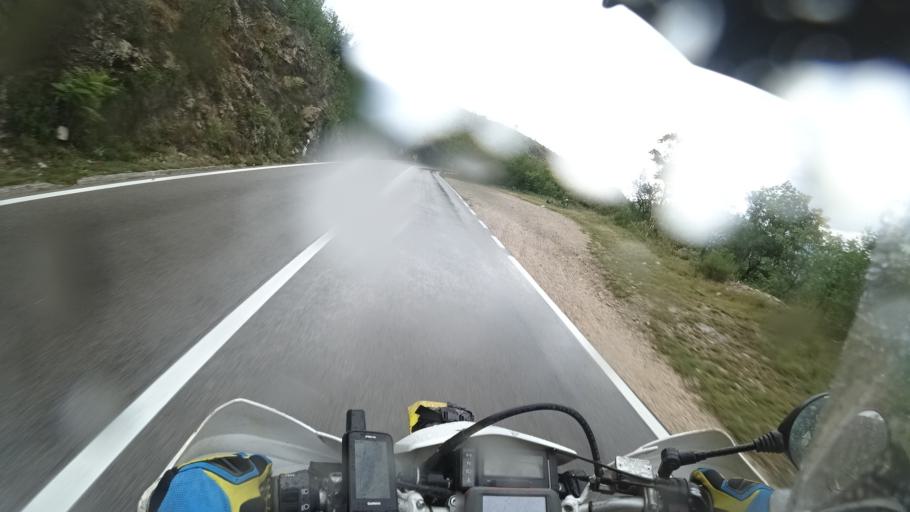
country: HR
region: Sibensko-Kniniska
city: Knin
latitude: 44.0456
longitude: 16.1883
